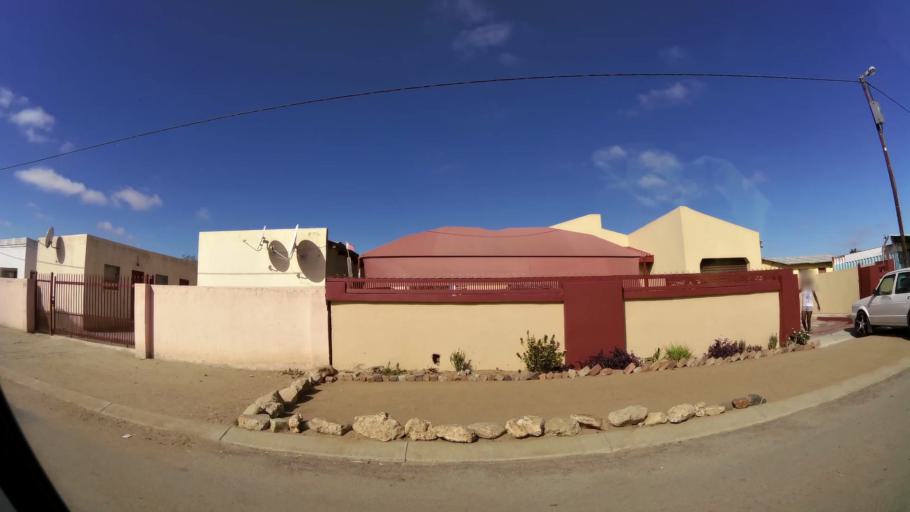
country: ZA
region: Limpopo
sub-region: Capricorn District Municipality
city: Polokwane
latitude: -23.8612
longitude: 29.3675
